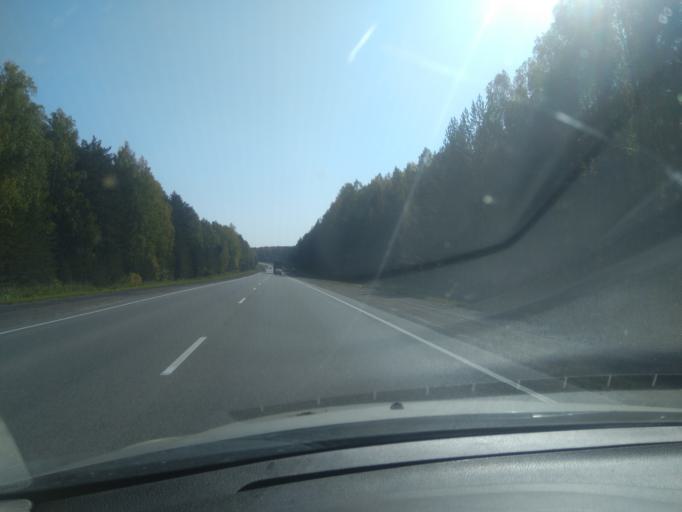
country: RU
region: Sverdlovsk
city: Verkhneye Dubrovo
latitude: 56.7120
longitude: 61.0626
